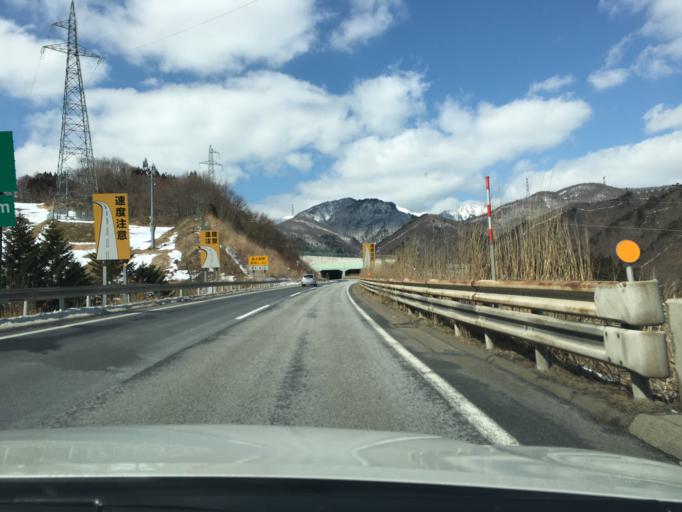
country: JP
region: Yamagata
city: Yamagata-shi
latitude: 38.2174
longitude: 140.5206
